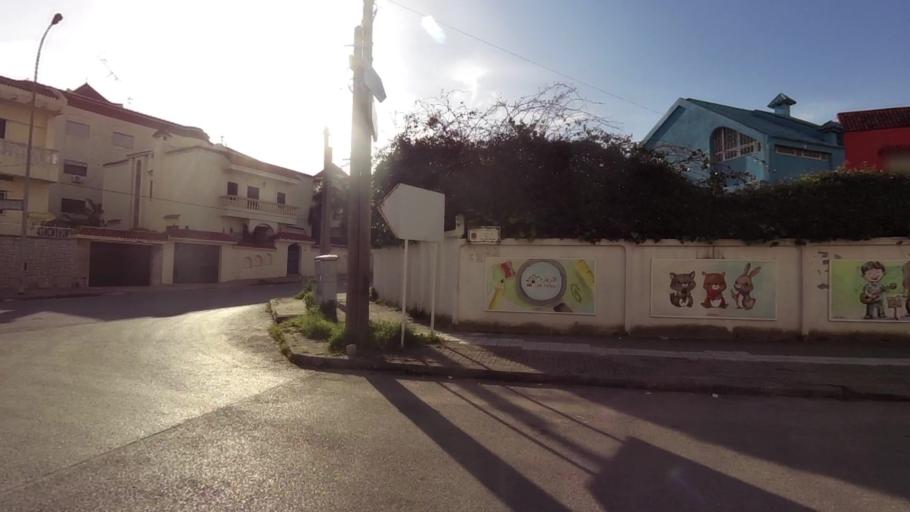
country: MA
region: Tanger-Tetouan
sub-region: Tanger-Assilah
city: Tangier
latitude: 35.7694
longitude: -5.7993
